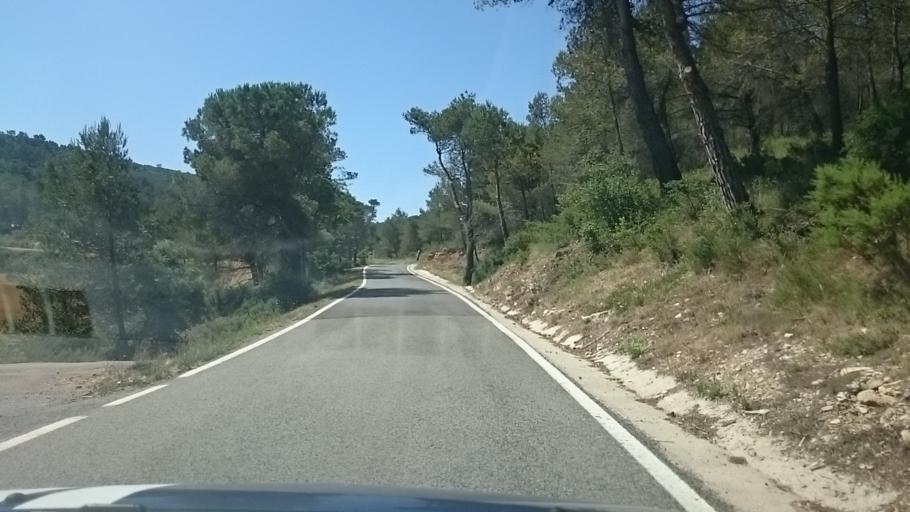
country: ES
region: Catalonia
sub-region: Provincia de Tarragona
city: Querol
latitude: 41.3905
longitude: 1.4335
